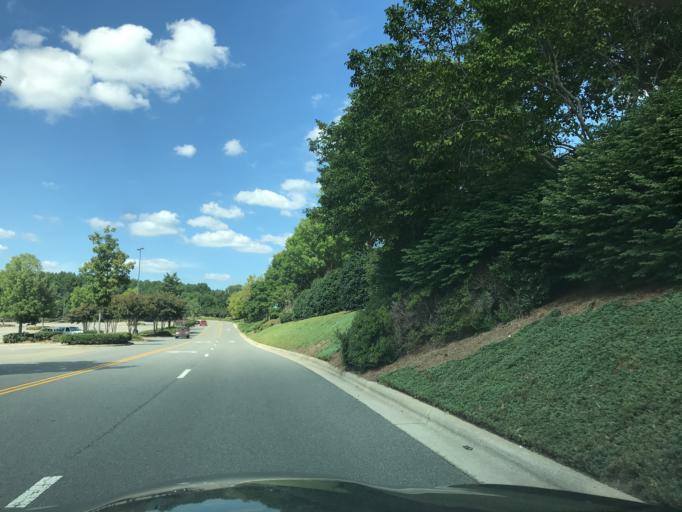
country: US
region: North Carolina
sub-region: Durham County
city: Durham
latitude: 35.9045
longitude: -78.9385
